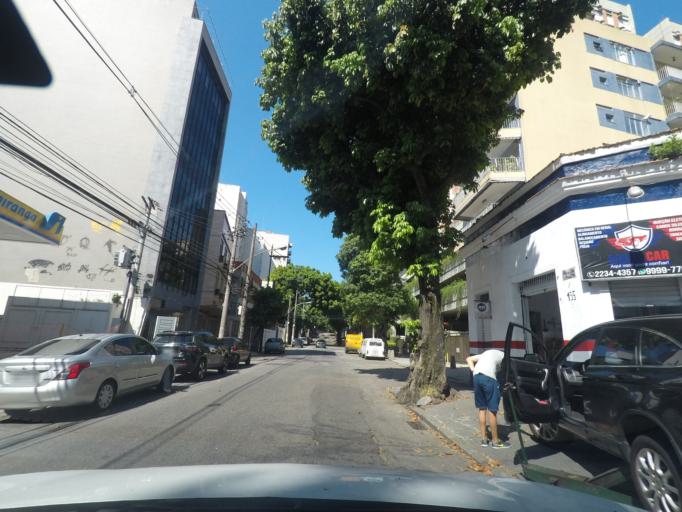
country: BR
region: Rio de Janeiro
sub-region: Rio De Janeiro
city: Rio de Janeiro
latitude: -22.9287
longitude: -43.2309
